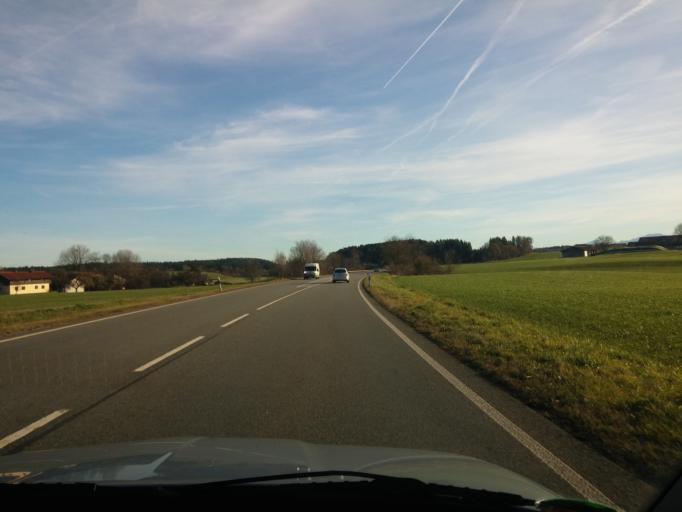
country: DE
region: Bavaria
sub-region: Upper Bavaria
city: Babensham
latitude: 48.0545
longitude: 12.2780
